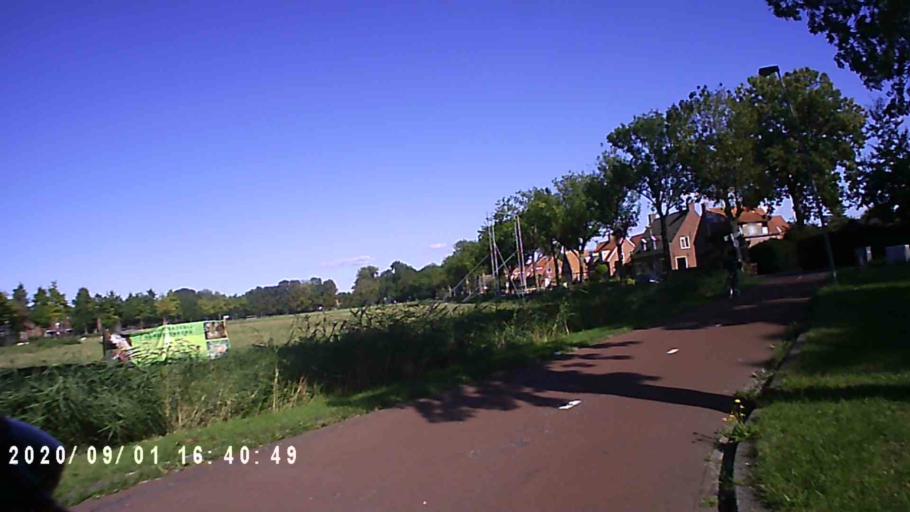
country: NL
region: Groningen
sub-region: Gemeente Groningen
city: Oosterpark
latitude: 53.2292
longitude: 6.5929
